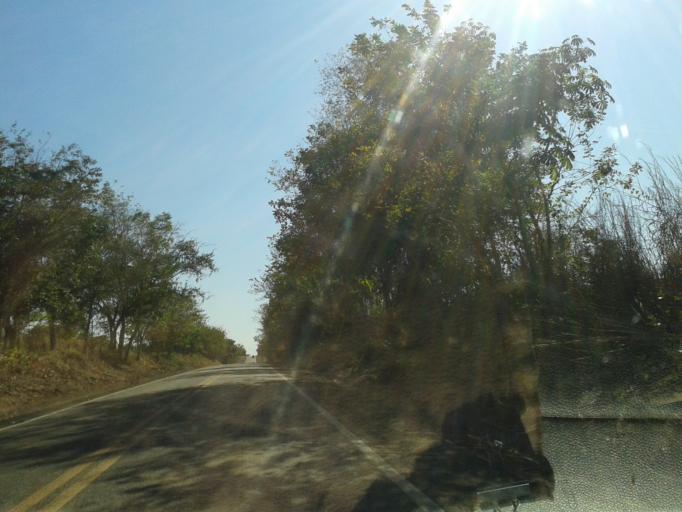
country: BR
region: Goias
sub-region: Mozarlandia
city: Mozarlandia
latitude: -14.5695
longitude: -50.5003
